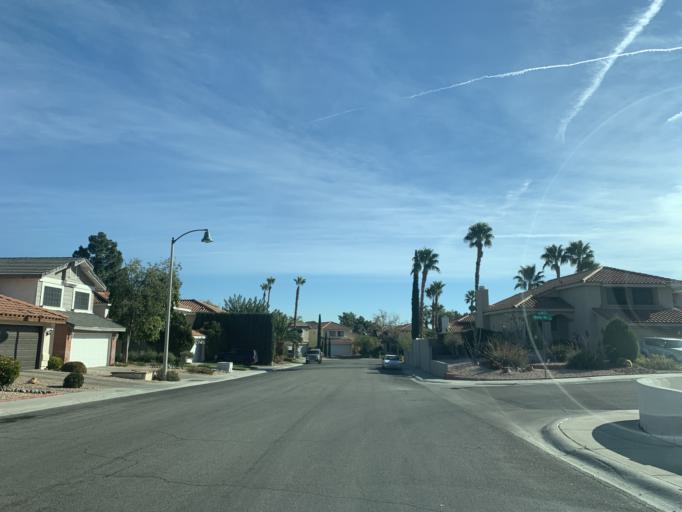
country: US
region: Nevada
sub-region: Clark County
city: Summerlin South
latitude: 36.1370
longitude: -115.2909
